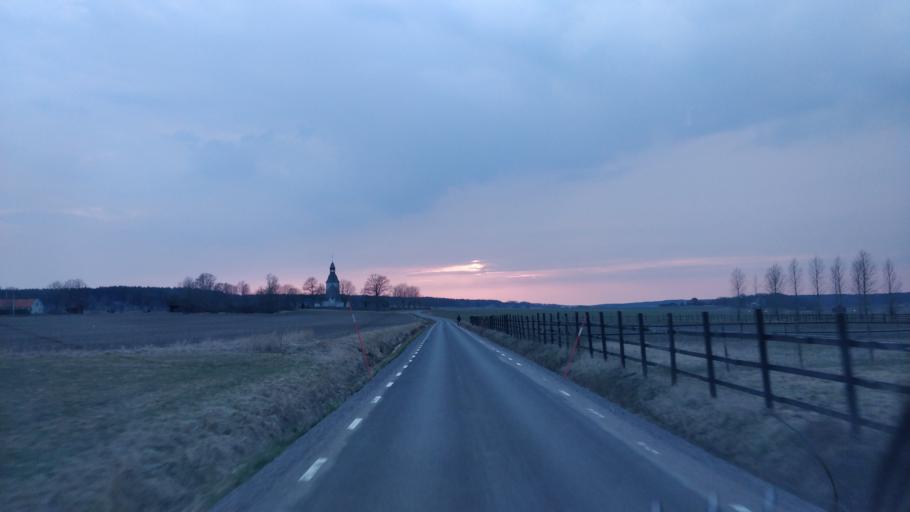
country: SE
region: Uppsala
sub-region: Enkopings Kommun
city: Orsundsbro
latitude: 59.7318
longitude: 17.2055
